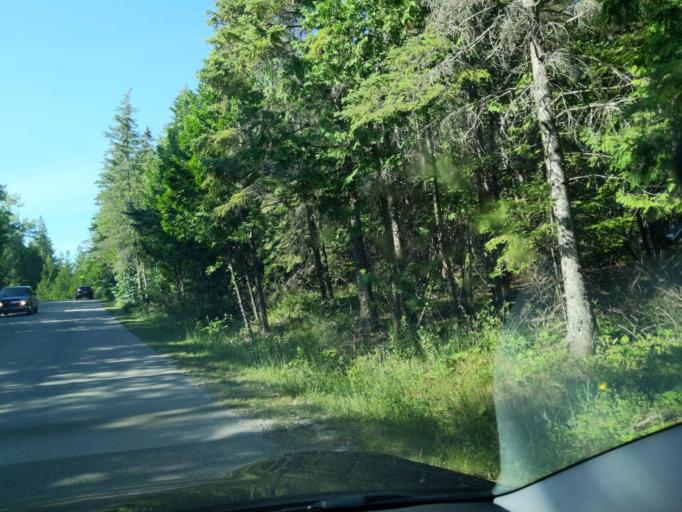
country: US
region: Michigan
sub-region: Mackinac County
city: Saint Ignace
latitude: 45.8516
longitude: -84.7185
